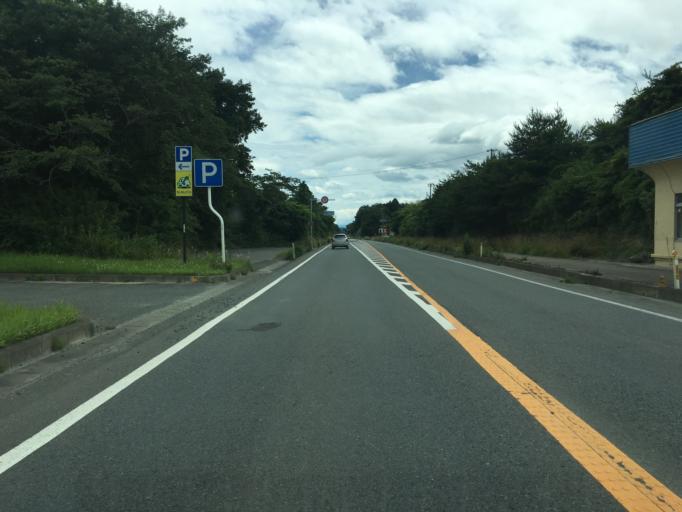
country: JP
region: Miyagi
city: Marumori
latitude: 37.7445
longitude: 140.9543
